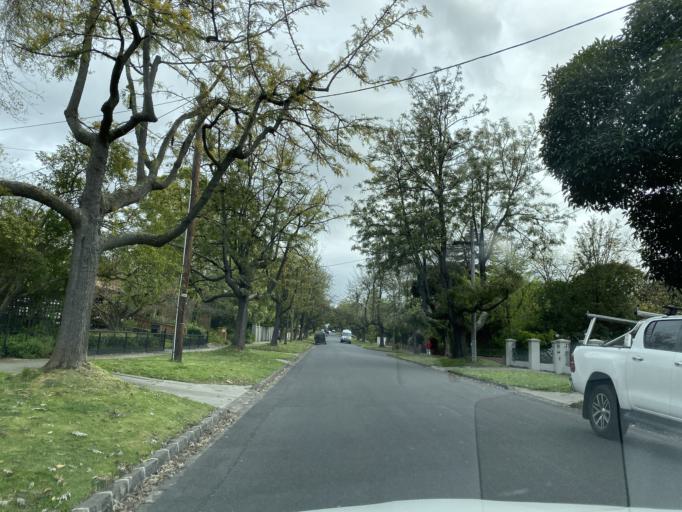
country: AU
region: Victoria
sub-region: Boroondara
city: Camberwell
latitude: -37.8402
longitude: 145.0803
